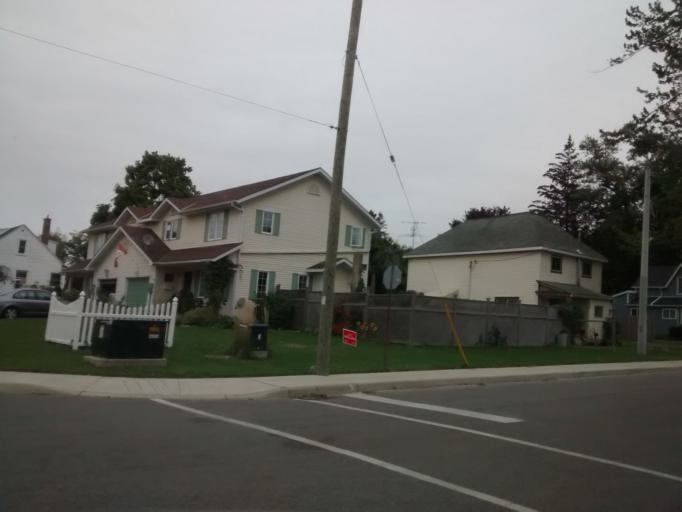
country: CA
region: Ontario
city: Welland
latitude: 42.9045
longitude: -79.6135
